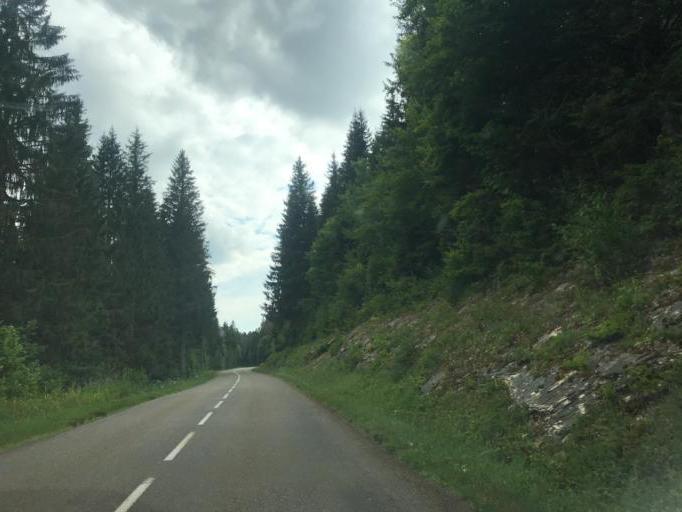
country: FR
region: Franche-Comte
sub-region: Departement du Jura
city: Valfin-les-Saint-Claude
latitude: 46.4963
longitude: 5.8521
